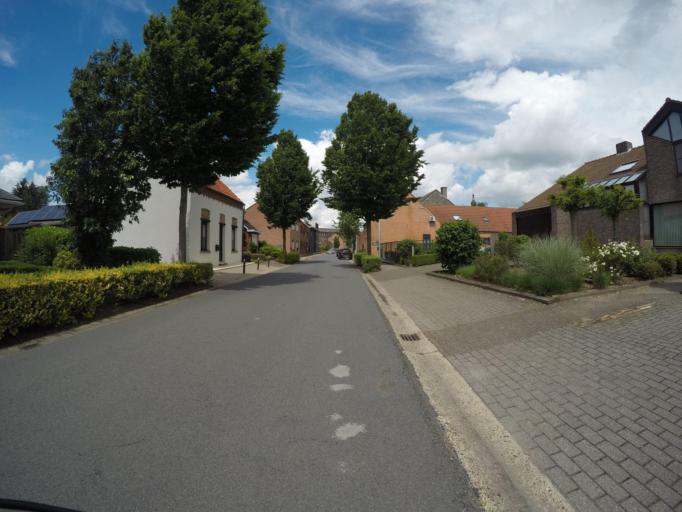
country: BE
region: Flanders
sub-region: Provincie Antwerpen
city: Hoogstraten
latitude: 51.3960
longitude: 4.7625
